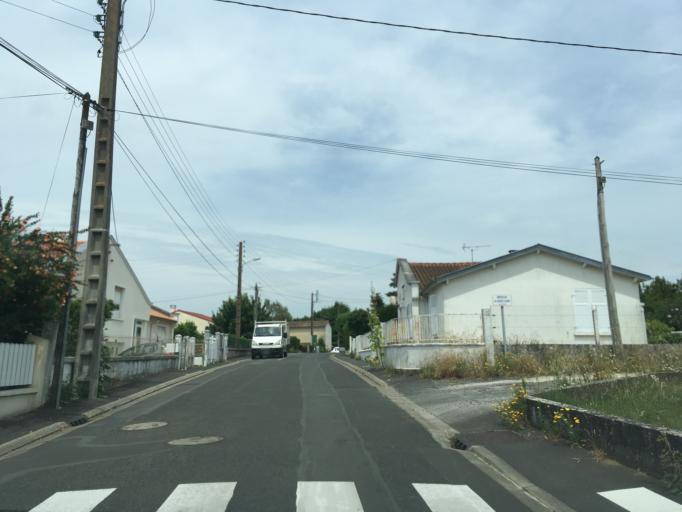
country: FR
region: Poitou-Charentes
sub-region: Departement des Deux-Sevres
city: Niort
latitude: 46.3218
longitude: -0.4855
